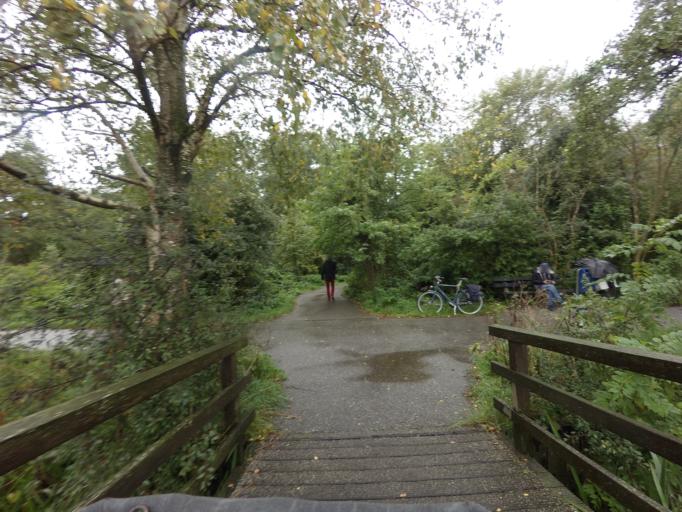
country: NL
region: Friesland
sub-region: Gemeente Leeuwarden
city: Bilgaard
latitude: 53.2181
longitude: 5.7922
